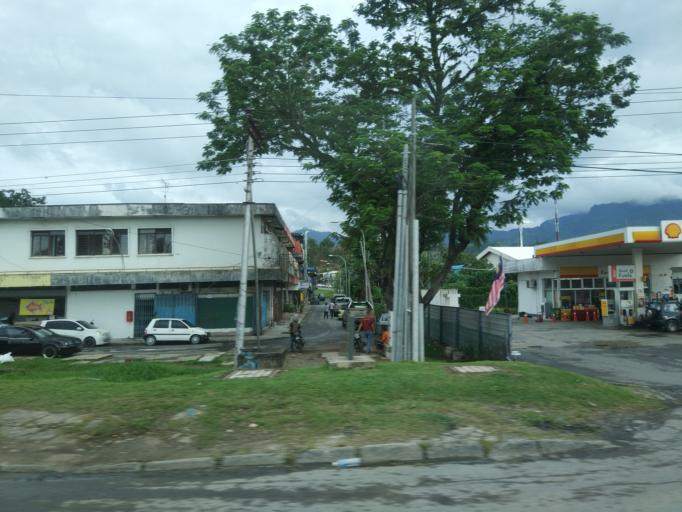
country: MY
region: Sabah
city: Kota Kinabalu
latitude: 6.0894
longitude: 116.1951
